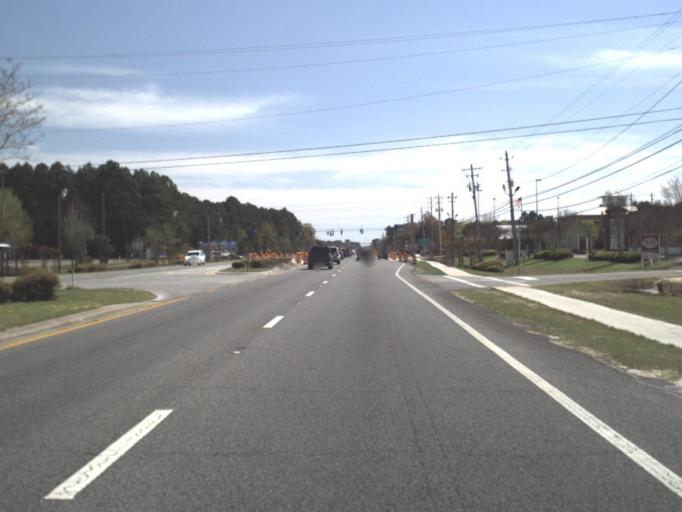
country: US
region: Florida
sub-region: Bay County
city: Hiland Park
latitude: 30.2045
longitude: -85.6498
